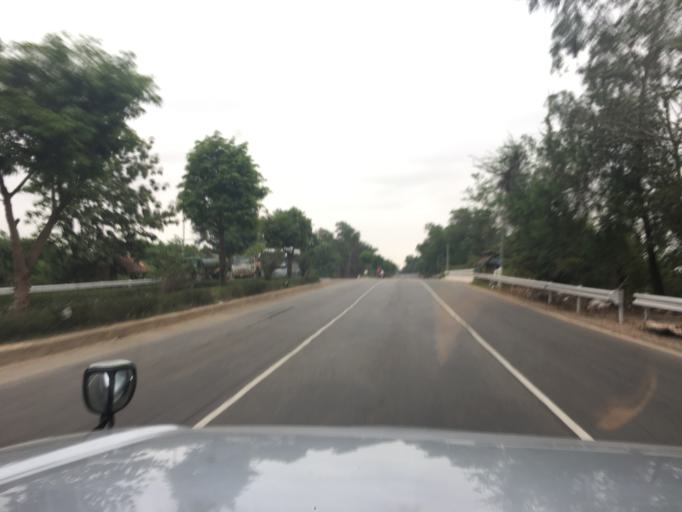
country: MM
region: Bago
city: Bago
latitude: 17.2267
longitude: 96.4522
